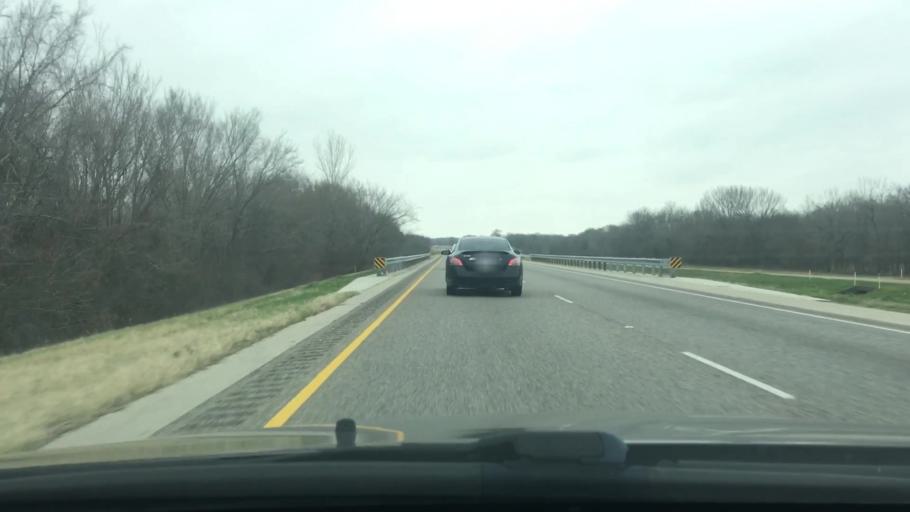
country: US
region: Texas
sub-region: Freestone County
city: Fairfield
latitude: 31.7989
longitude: -96.2569
